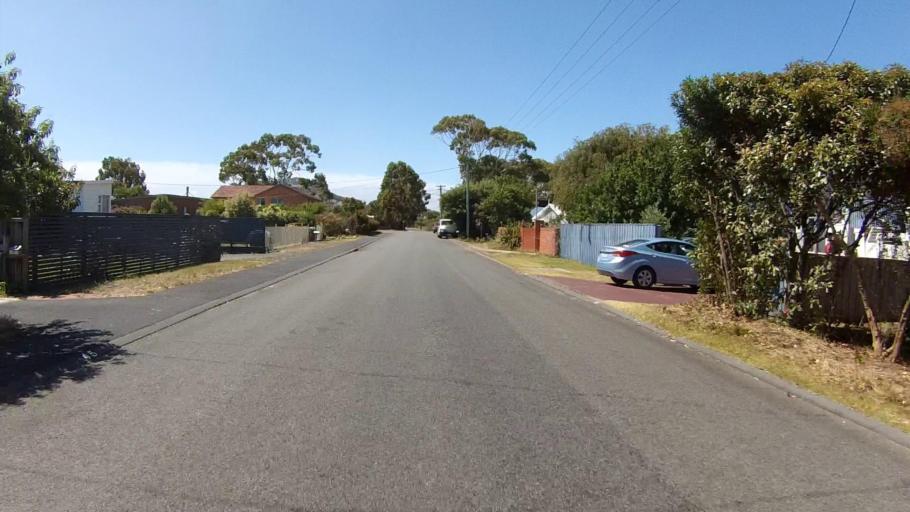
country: AU
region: Tasmania
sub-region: Clarence
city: Lauderdale
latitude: -42.8985
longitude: 147.4969
